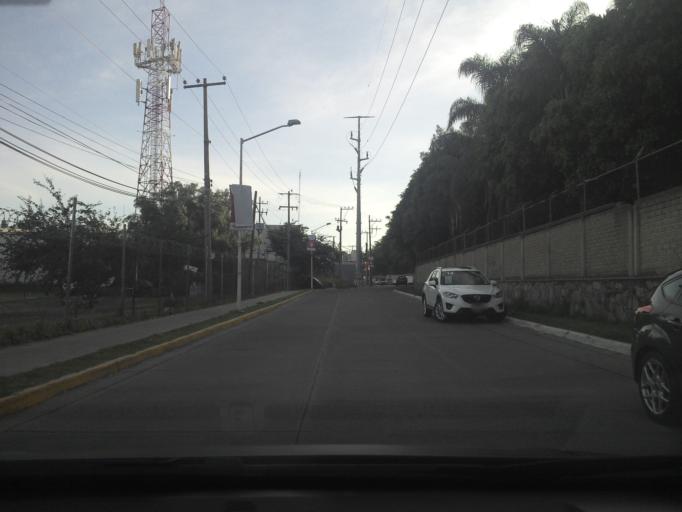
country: MX
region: Jalisco
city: Tlaquepaque
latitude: 20.6196
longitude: -103.3255
